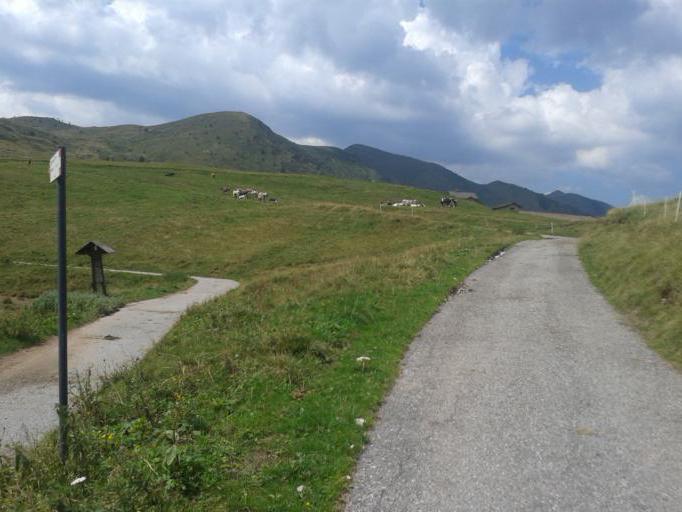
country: IT
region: Trentino-Alto Adige
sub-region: Provincia di Trento
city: Lodrone-Darzo
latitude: 45.8728
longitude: 10.5226
